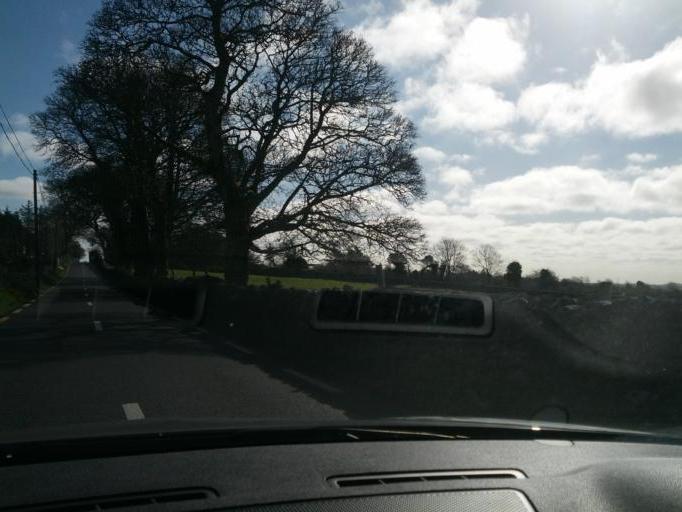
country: IE
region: Connaught
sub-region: County Galway
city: Ballinasloe
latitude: 53.3923
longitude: -8.3198
